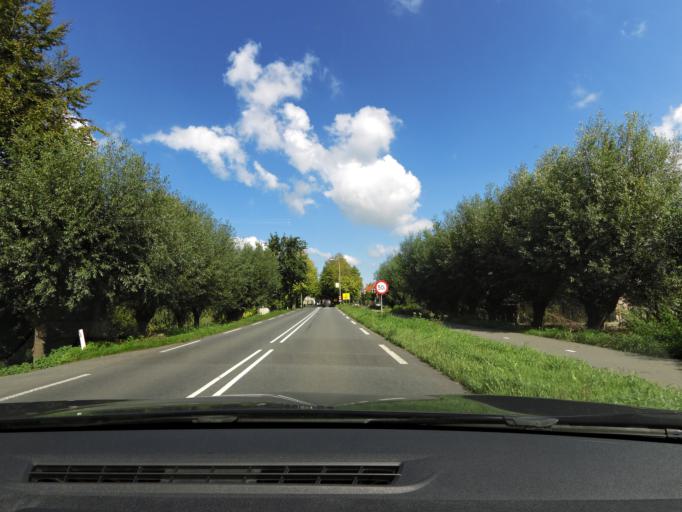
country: NL
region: South Holland
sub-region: Gemeente Alphen aan den Rijn
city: Alphen aan den Rijn
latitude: 52.1634
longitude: 4.7098
